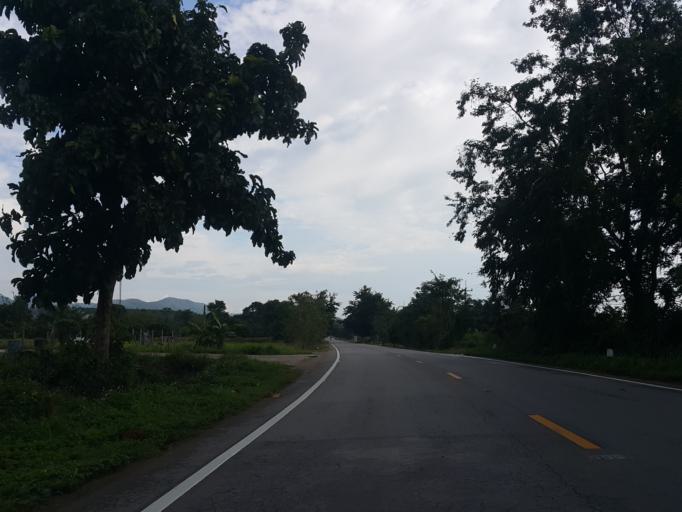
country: TH
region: Chiang Mai
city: Phrao
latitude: 19.2493
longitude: 99.1843
